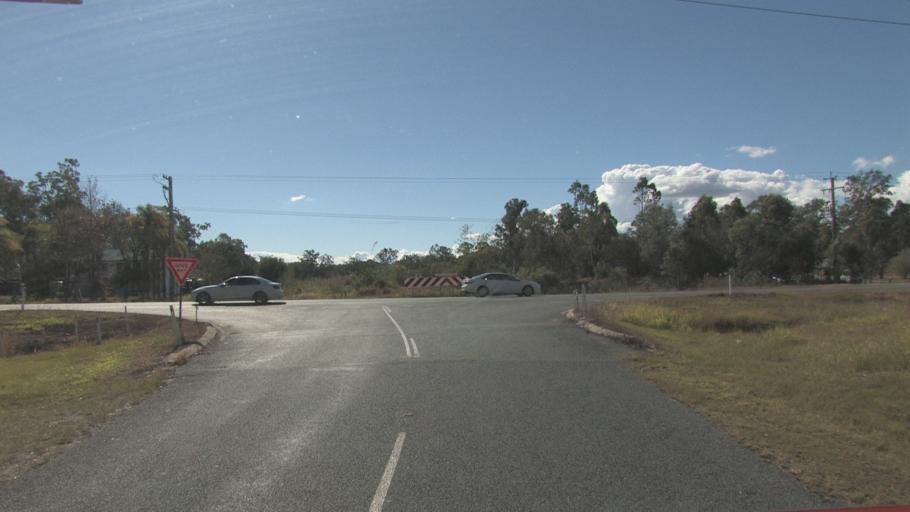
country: AU
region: Queensland
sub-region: Logan
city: Chambers Flat
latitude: -27.8046
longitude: 153.0730
